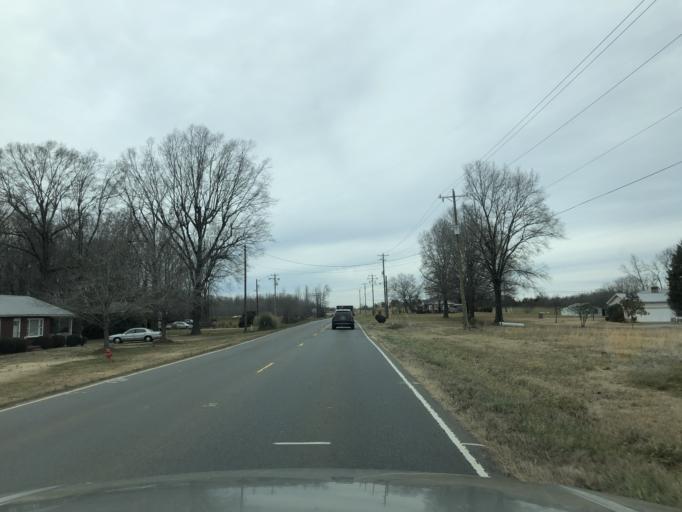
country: US
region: North Carolina
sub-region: Cleveland County
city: Shelby
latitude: 35.3079
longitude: -81.4875
